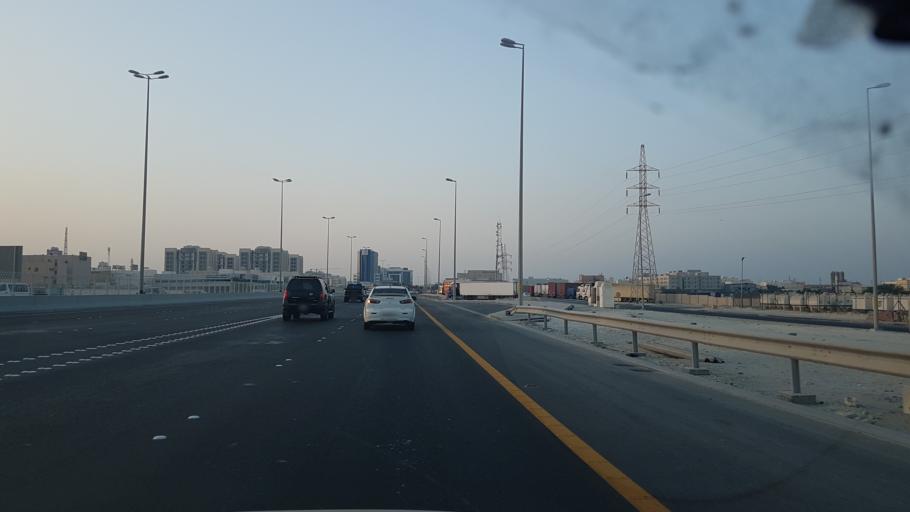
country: BH
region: Northern
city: Ar Rifa'
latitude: 26.1289
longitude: 50.5882
